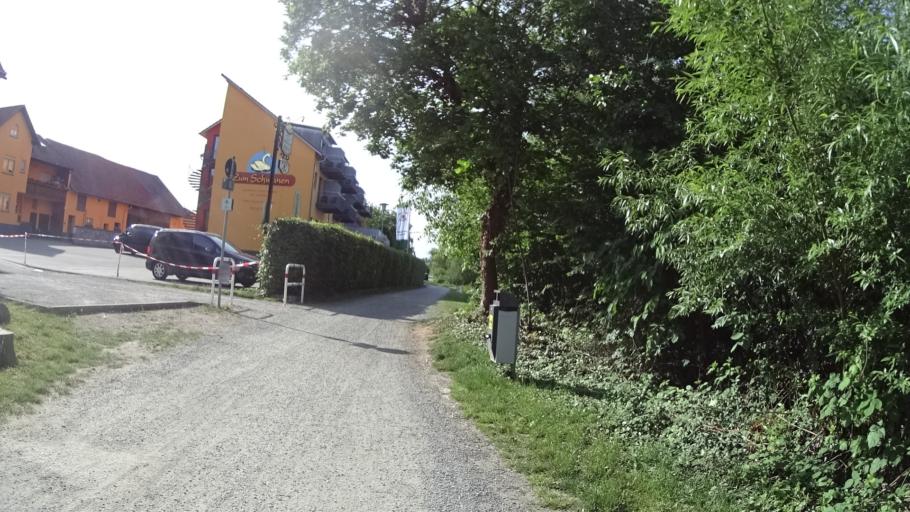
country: DE
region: Bavaria
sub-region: Regierungsbezirk Unterfranken
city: Kleinostheim
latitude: 49.9986
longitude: 9.0612
